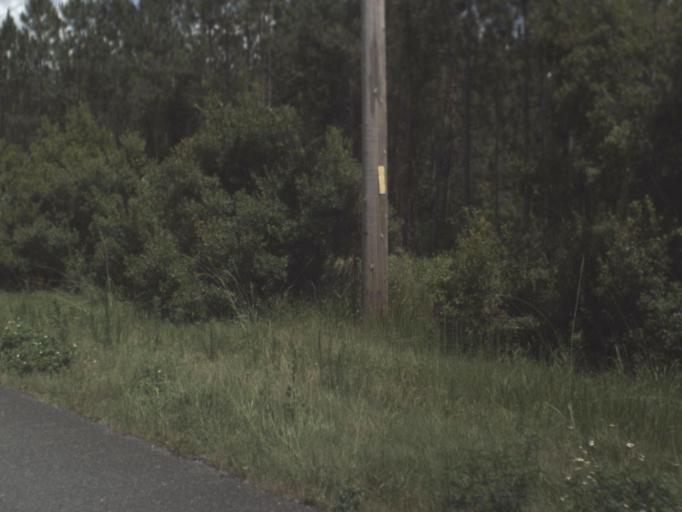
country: US
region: Florida
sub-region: Gilchrist County
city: Trenton
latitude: 29.6181
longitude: -82.7797
